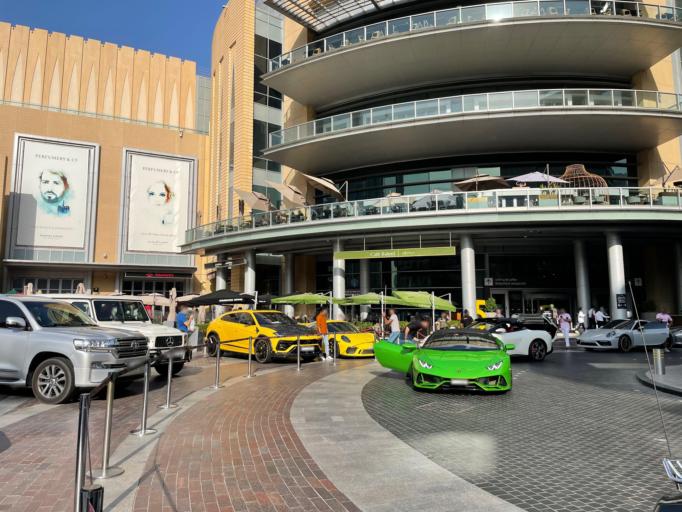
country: AE
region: Dubai
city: Dubai
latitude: 25.1949
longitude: 55.2787
